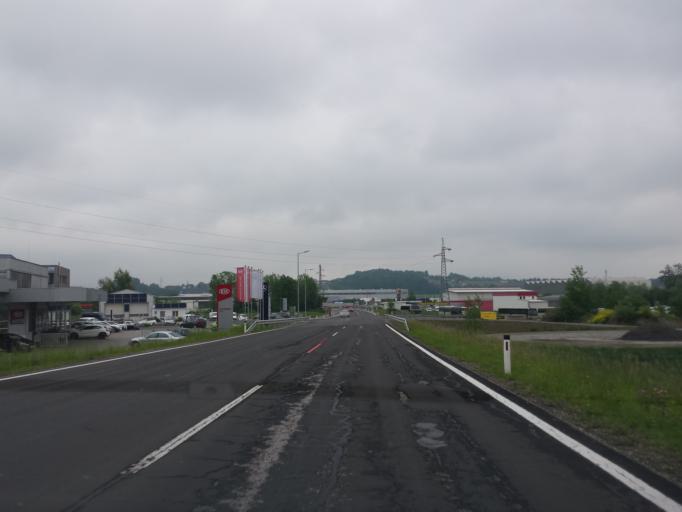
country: AT
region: Styria
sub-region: Politischer Bezirk Weiz
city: Krottendorf
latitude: 47.2045
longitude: 15.6340
